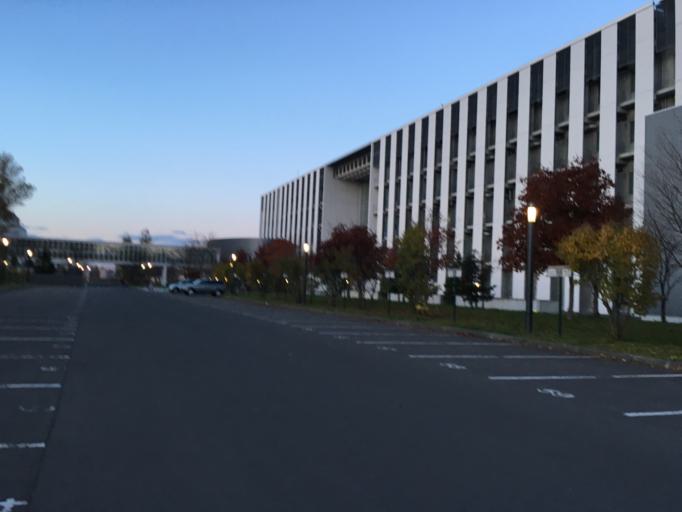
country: JP
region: Hokkaido
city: Sapporo
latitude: 43.0835
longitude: 141.3353
